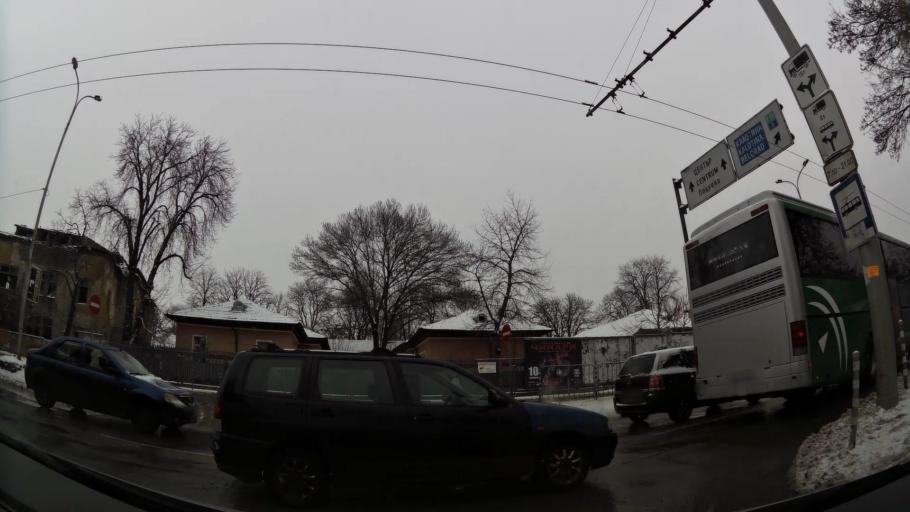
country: BG
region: Sofia-Capital
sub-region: Stolichna Obshtina
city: Sofia
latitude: 42.7060
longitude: 23.3325
